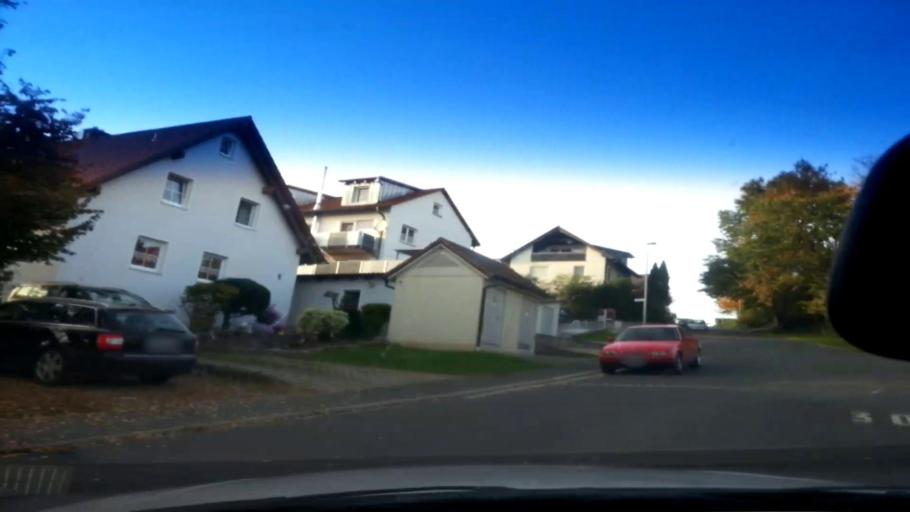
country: DE
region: Bavaria
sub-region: Upper Franconia
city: Memmelsdorf
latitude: 49.9418
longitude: 10.9542
